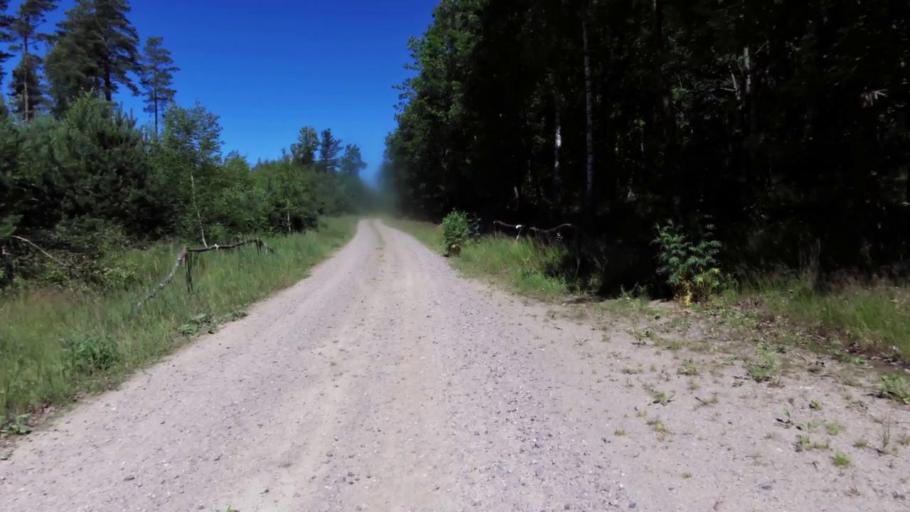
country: PL
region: West Pomeranian Voivodeship
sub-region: Powiat swidwinski
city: Rabino
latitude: 53.8658
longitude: 16.0342
